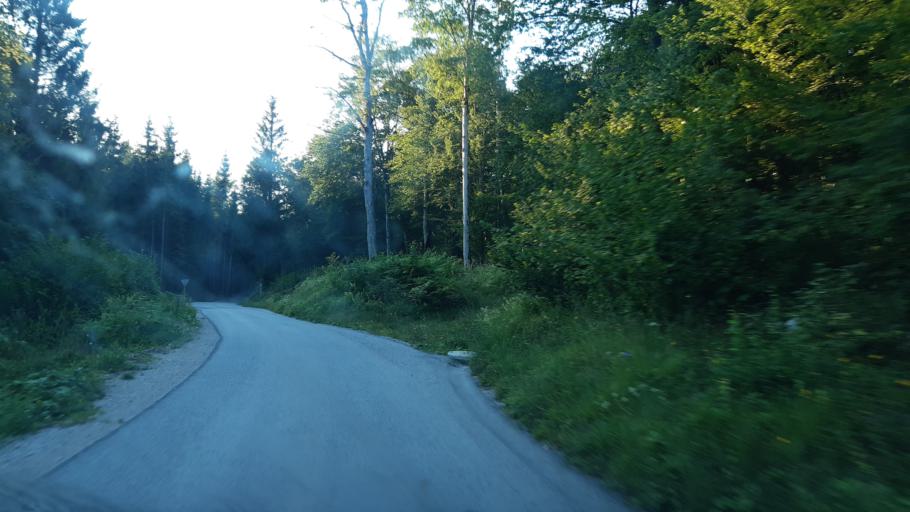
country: SI
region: Kocevje
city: Kocevje
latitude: 45.6683
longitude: 14.9208
